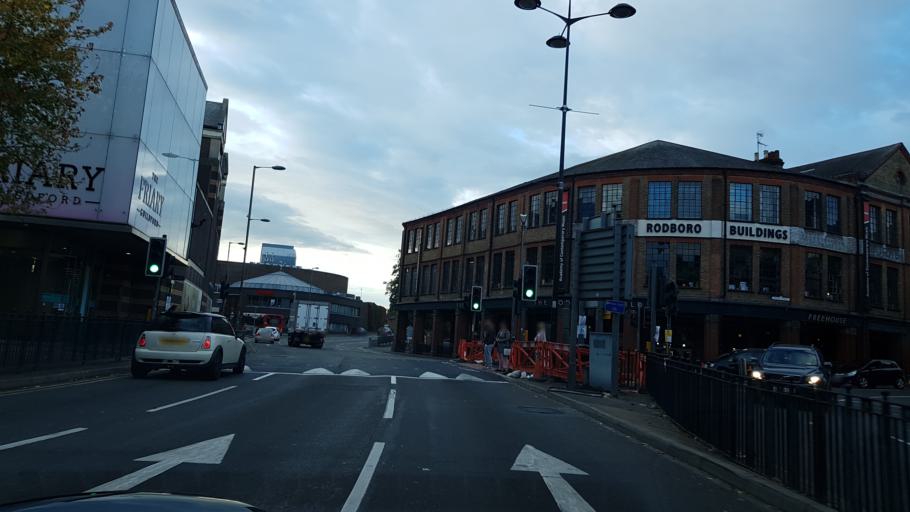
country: GB
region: England
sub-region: Surrey
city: Guildford
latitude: 51.2372
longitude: -0.5772
